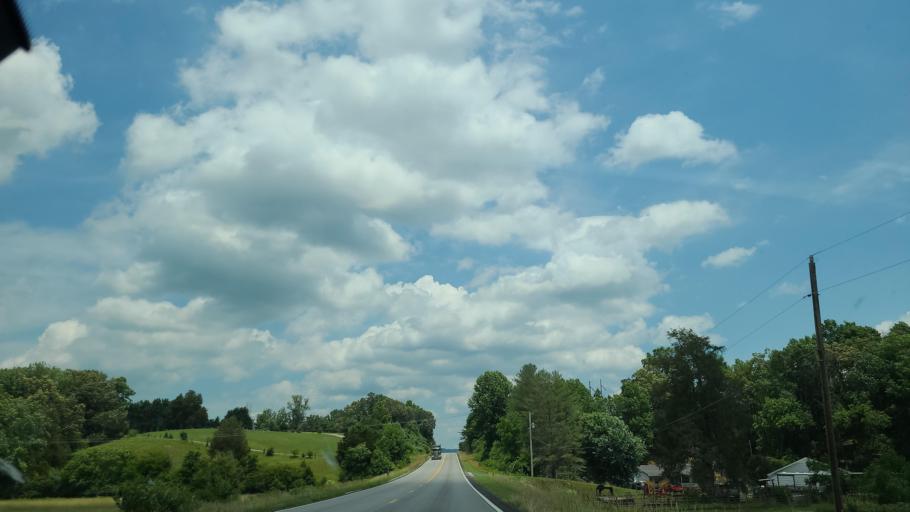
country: US
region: Tennessee
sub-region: Bledsoe County
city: Pikeville
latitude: 35.7080
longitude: -85.1012
